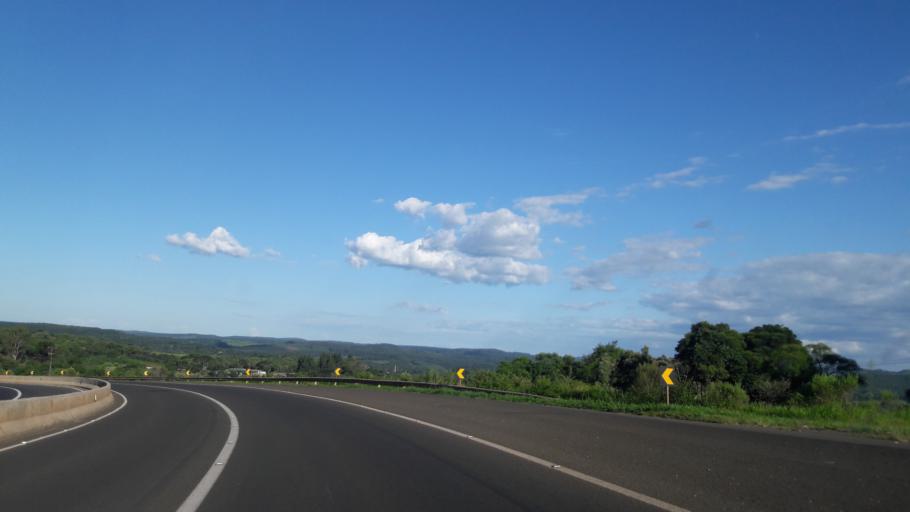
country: BR
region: Parana
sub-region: Guarapuava
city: Guarapuava
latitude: -25.3487
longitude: -51.3902
